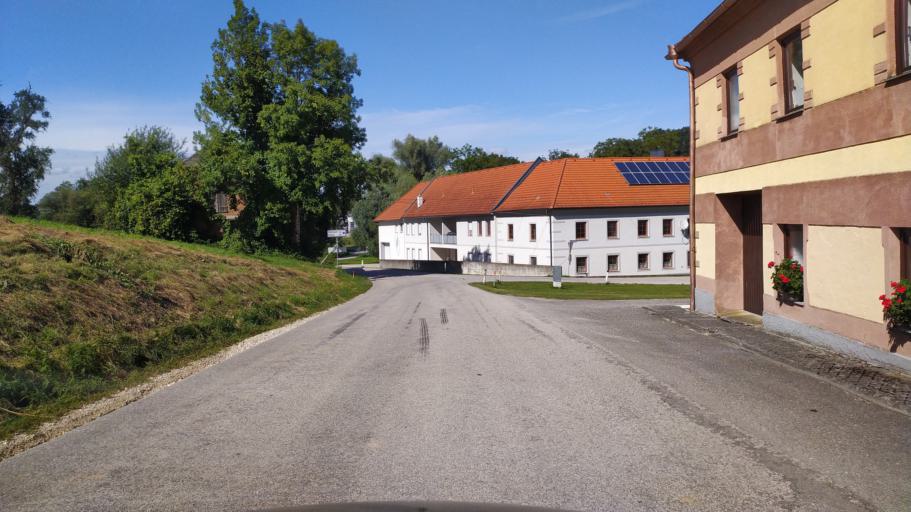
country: AT
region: Lower Austria
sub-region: Politischer Bezirk Amstetten
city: Strengberg
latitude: 48.1352
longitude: 14.6739
